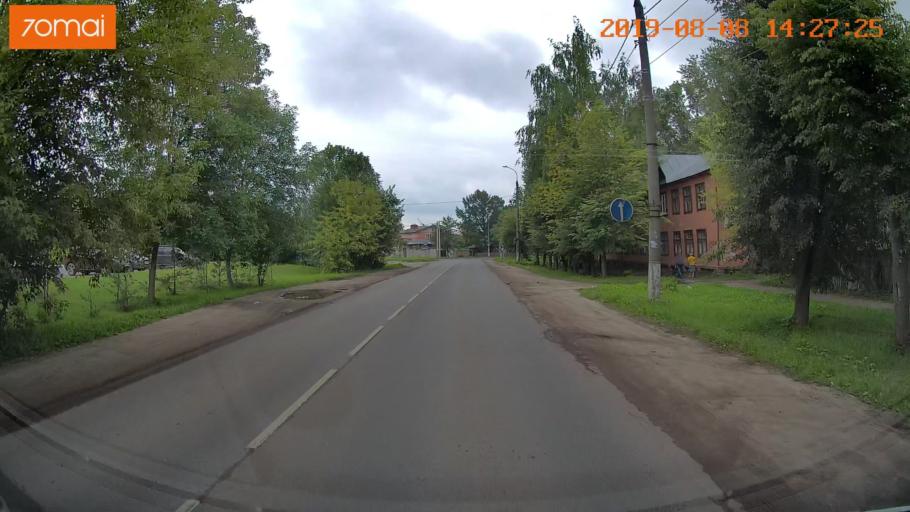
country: RU
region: Ivanovo
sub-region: Gorod Ivanovo
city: Ivanovo
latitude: 56.9973
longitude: 40.9412
